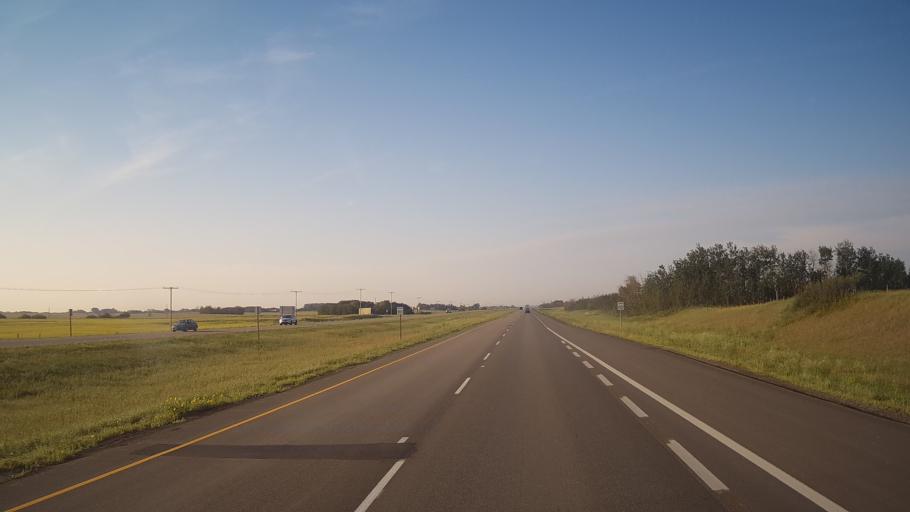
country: CA
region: Saskatchewan
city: Saskatoon
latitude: 52.0444
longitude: -106.5922
